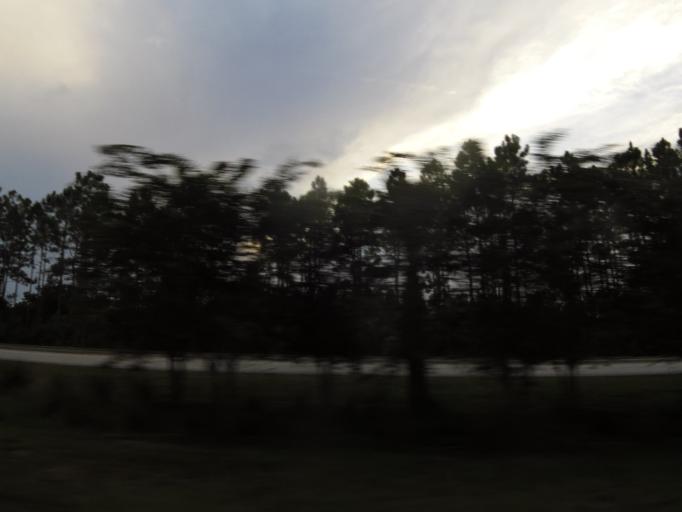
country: US
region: Florida
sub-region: Saint Johns County
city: Fruit Cove
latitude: 30.0811
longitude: -81.6031
